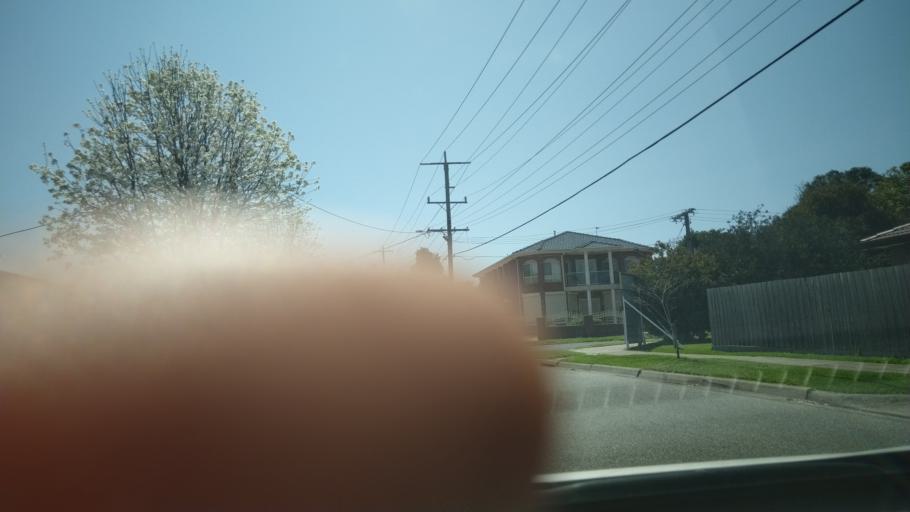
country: AU
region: Victoria
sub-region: Greater Dandenong
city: Noble Park
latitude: -37.9698
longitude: 145.1607
